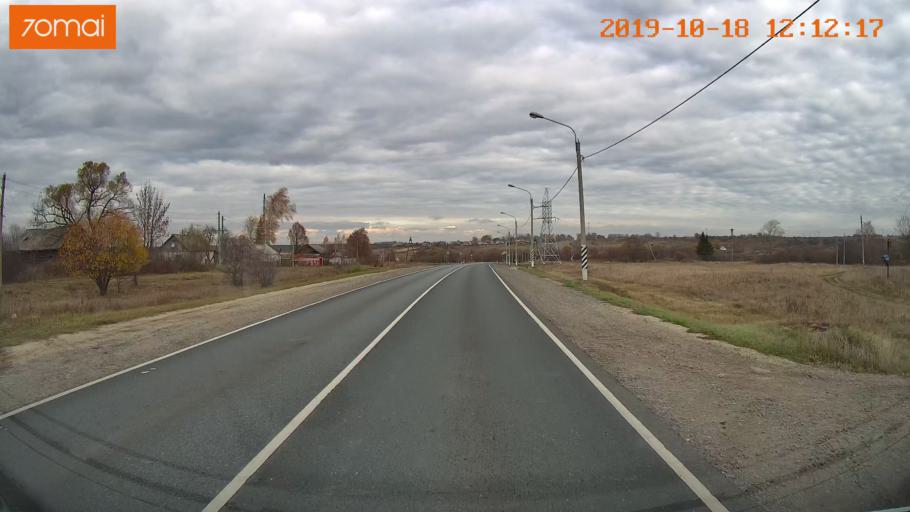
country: RU
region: Rjazan
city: Zakharovo
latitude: 54.4101
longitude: 39.3568
